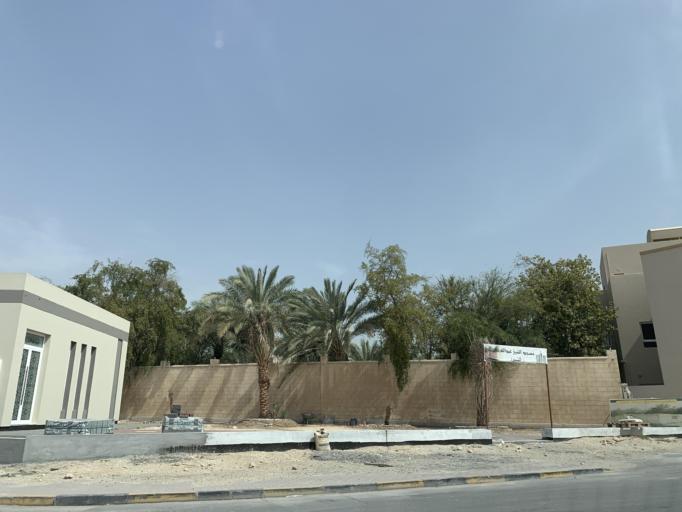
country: BH
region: Northern
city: Madinat `Isa
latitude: 26.1730
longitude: 50.5703
